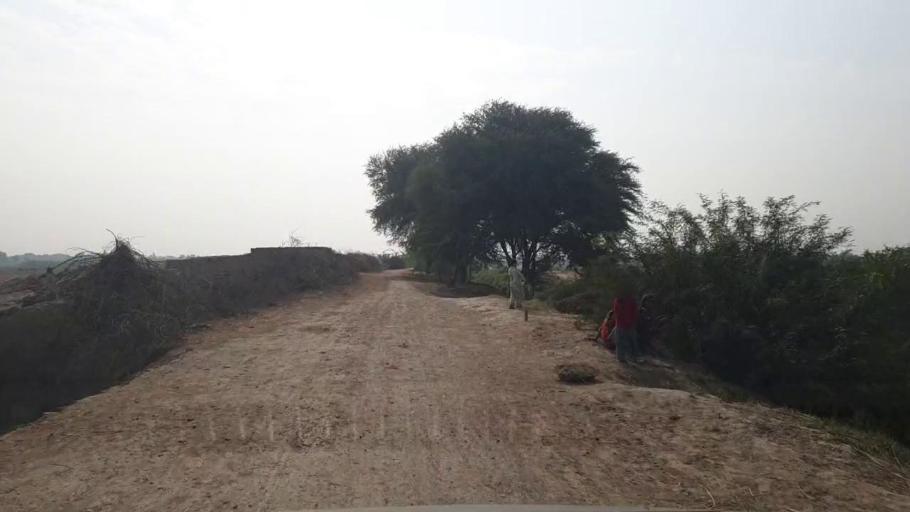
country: PK
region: Sindh
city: Tando Muhammad Khan
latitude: 25.1229
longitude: 68.4920
